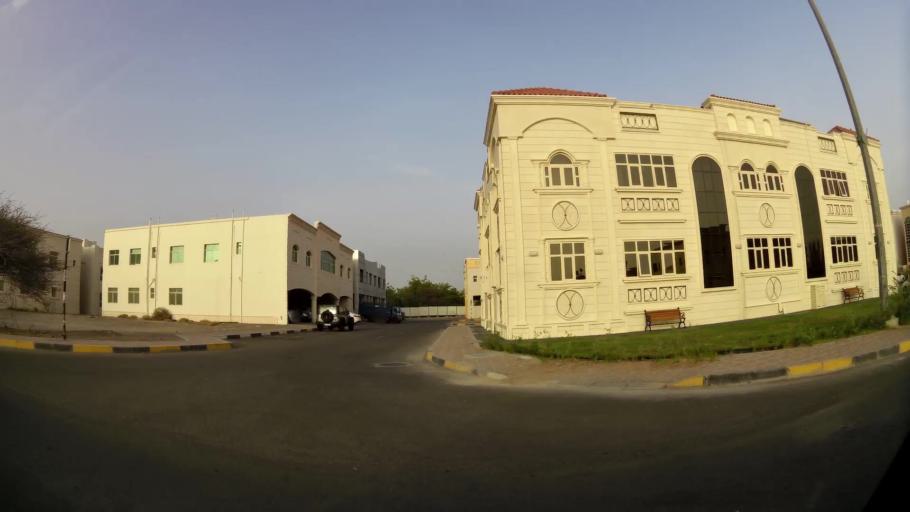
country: OM
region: Al Buraimi
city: Al Buraymi
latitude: 24.2457
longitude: 55.7342
